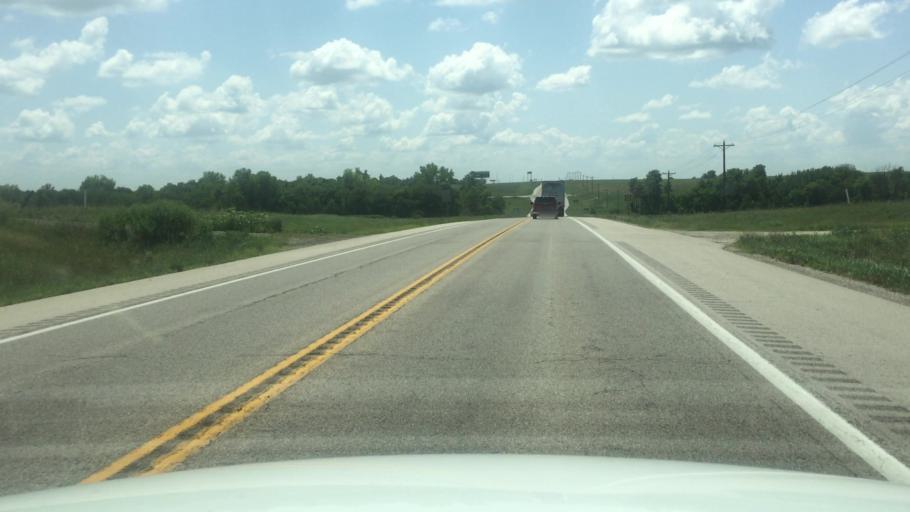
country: US
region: Kansas
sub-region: Brown County
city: Horton
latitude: 39.6722
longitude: -95.7307
